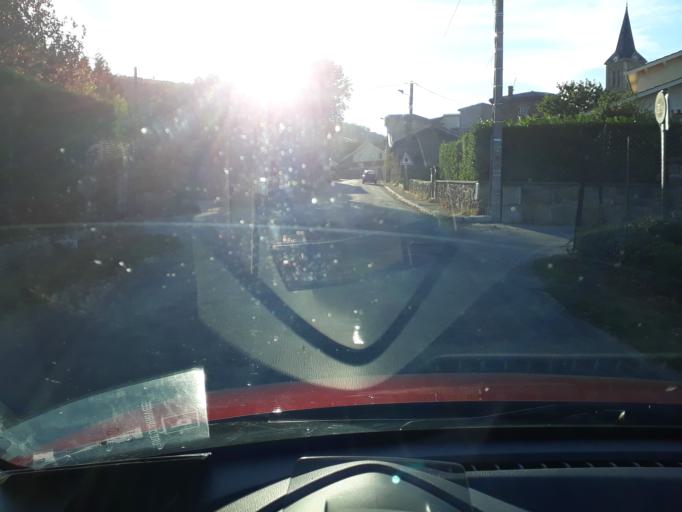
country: FR
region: Rhone-Alpes
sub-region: Departement de l'Ardeche
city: Felines
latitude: 45.3166
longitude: 4.7301
